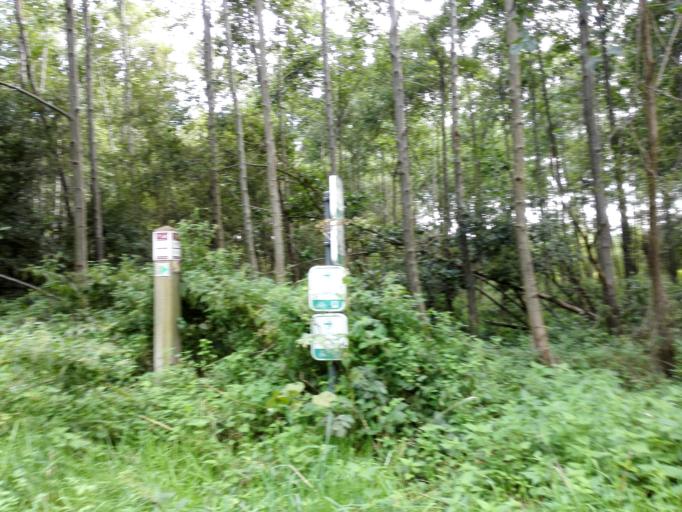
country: BE
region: Flanders
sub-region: Provincie Vlaams-Brabant
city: Oud-Heverlee
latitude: 50.8506
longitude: 4.6654
